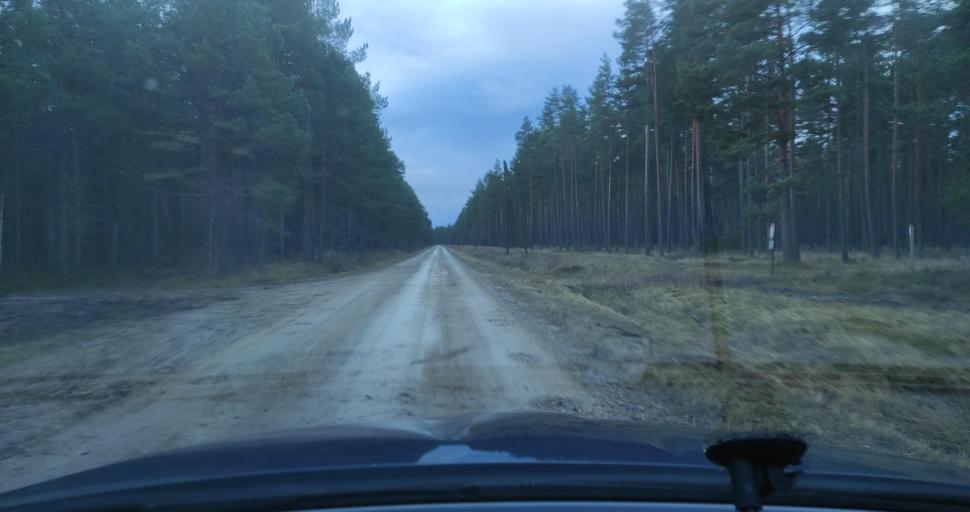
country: LV
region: Pavilostas
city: Pavilosta
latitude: 56.8013
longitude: 21.0669
